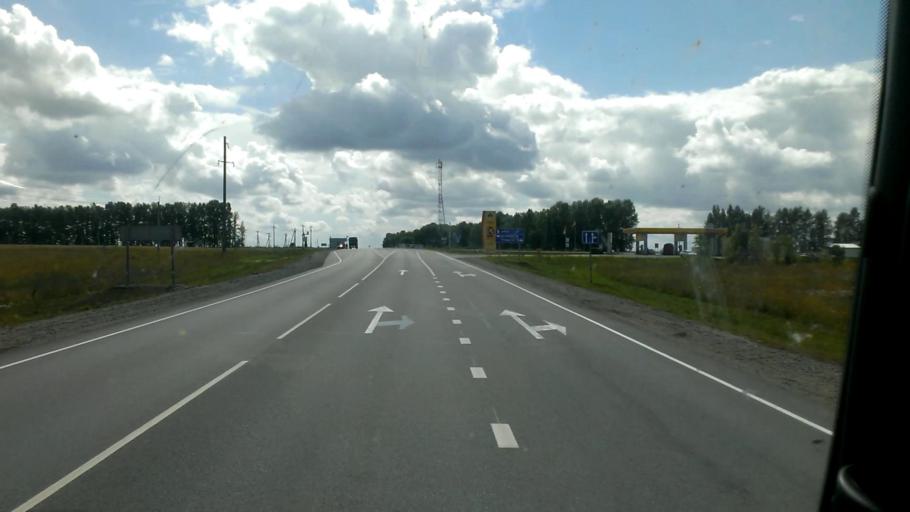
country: RU
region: Altai Krai
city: Troitskoye
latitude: 52.9695
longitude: 84.7492
